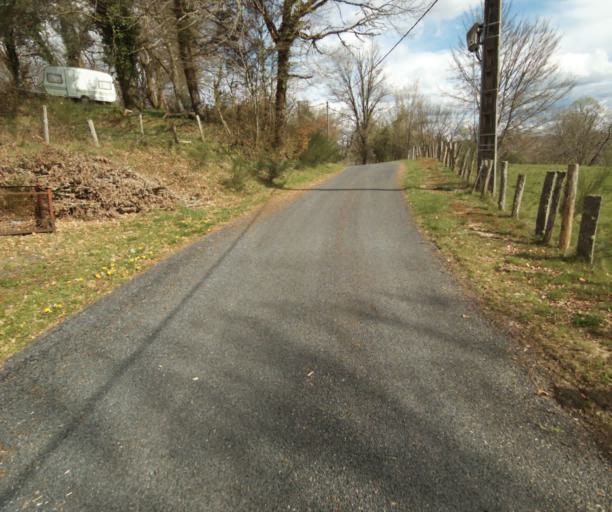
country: FR
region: Limousin
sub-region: Departement de la Correze
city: Argentat
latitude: 45.1844
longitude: 1.9494
